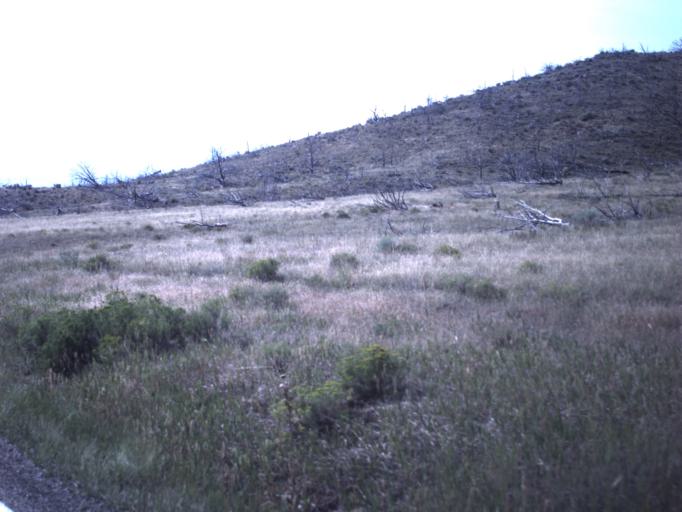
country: US
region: Utah
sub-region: Daggett County
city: Manila
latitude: 40.9503
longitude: -109.4458
